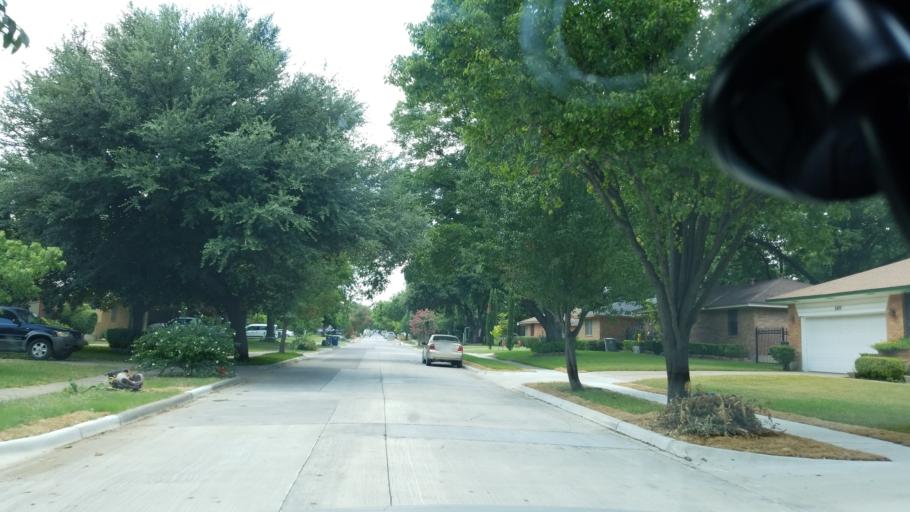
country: US
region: Texas
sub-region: Dallas County
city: Cockrell Hill
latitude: 32.7283
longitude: -96.8581
